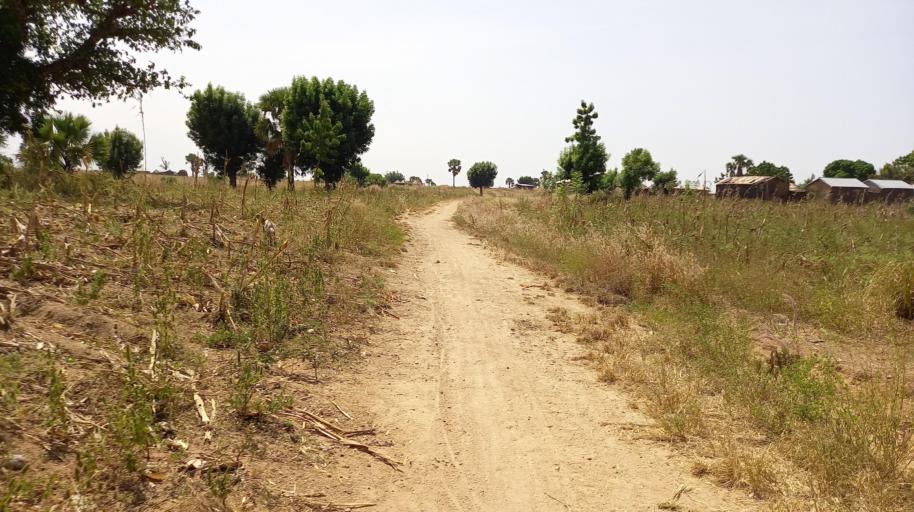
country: TG
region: Savanes
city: Dapaong
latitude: 10.9388
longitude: 0.3844
